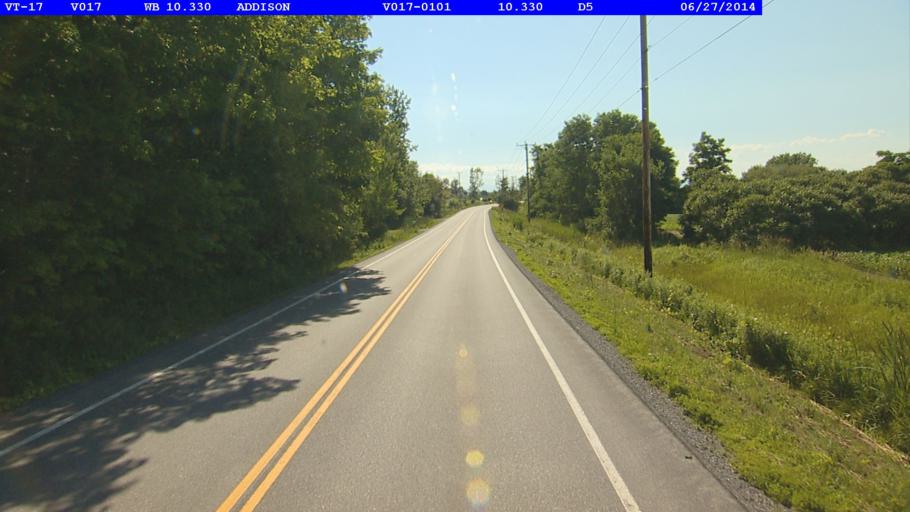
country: US
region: Vermont
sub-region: Addison County
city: Vergennes
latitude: 44.0823
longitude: -73.2661
